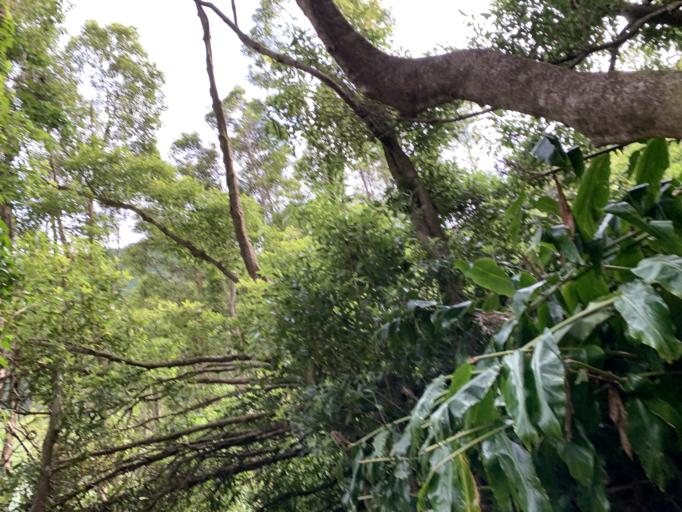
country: PT
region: Azores
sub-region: Ponta Delgada
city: Arrifes
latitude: 37.8521
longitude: -25.7738
